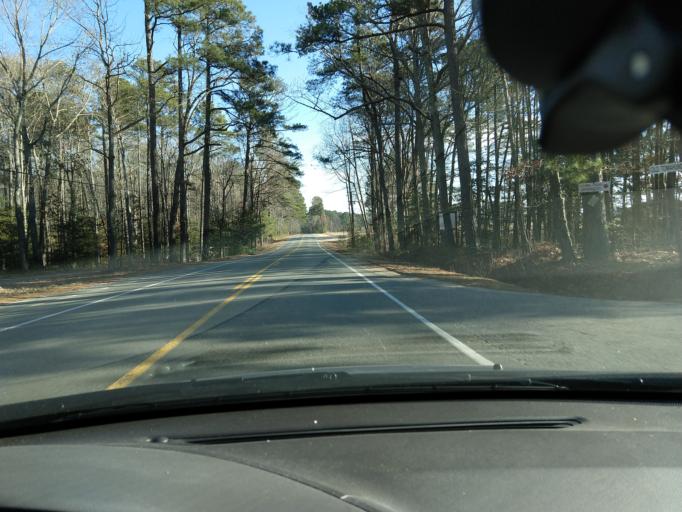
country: US
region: Virginia
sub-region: Surry County
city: Surry
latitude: 37.2670
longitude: -76.8965
